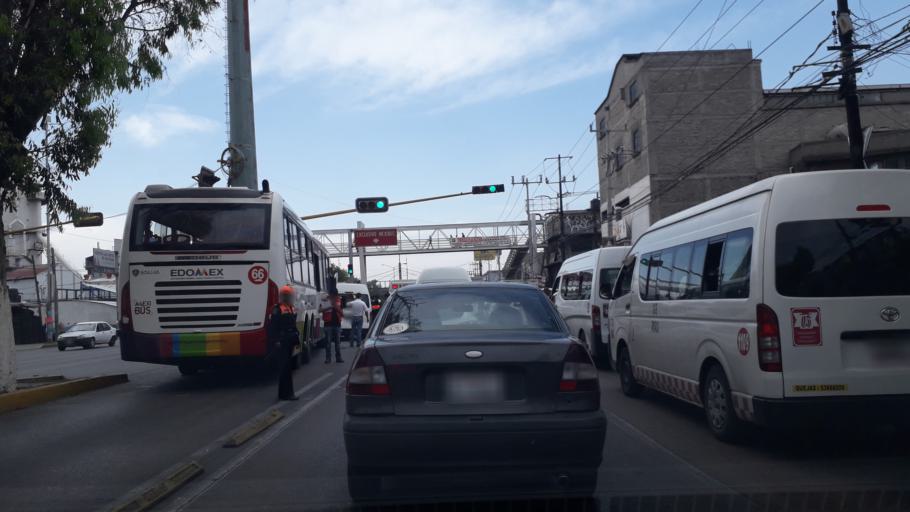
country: MX
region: Mexico
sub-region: Tultitlan
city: Buenavista
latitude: 19.6125
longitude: -99.1811
